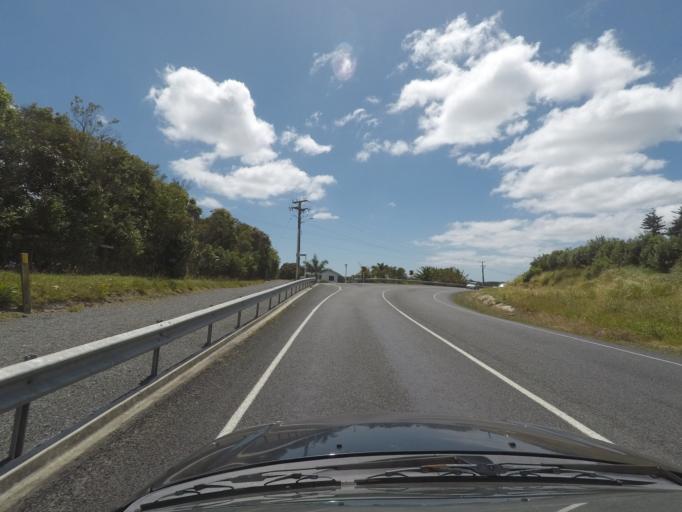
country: NZ
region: Northland
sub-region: Whangarei
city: Ruakaka
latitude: -35.9932
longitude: 174.4681
